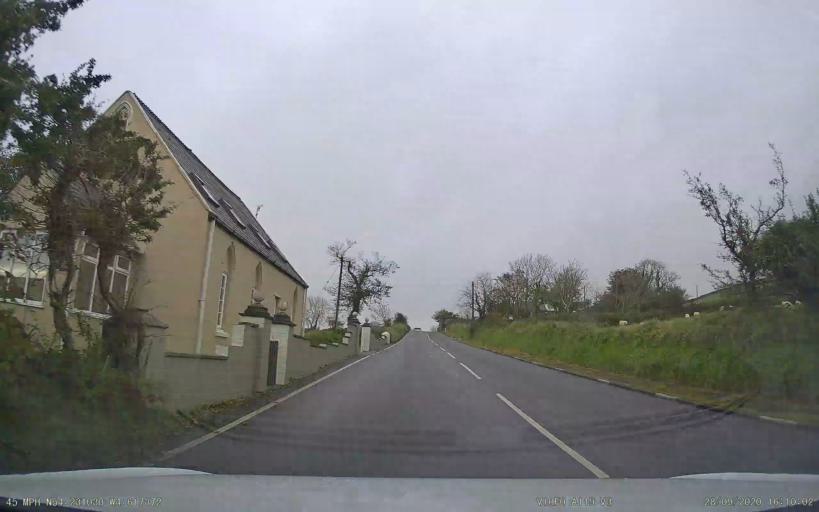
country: IM
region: Douglas
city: Douglas
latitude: 54.2310
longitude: -4.6174
